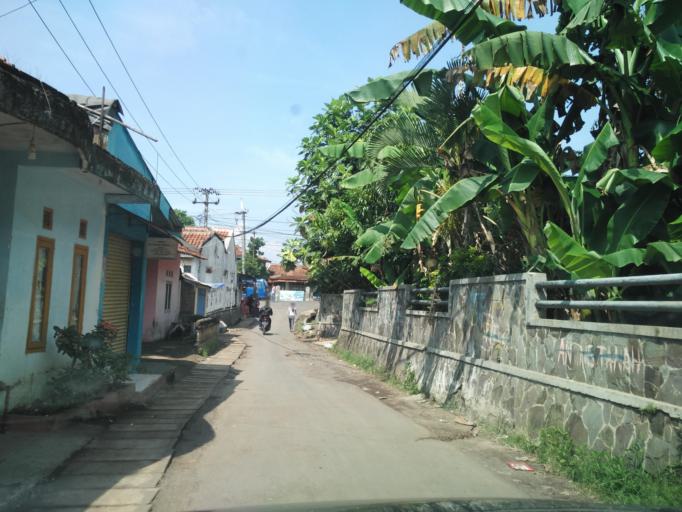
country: ID
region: West Java
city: Ciranjang-hilir
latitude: -6.8024
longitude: 107.1107
